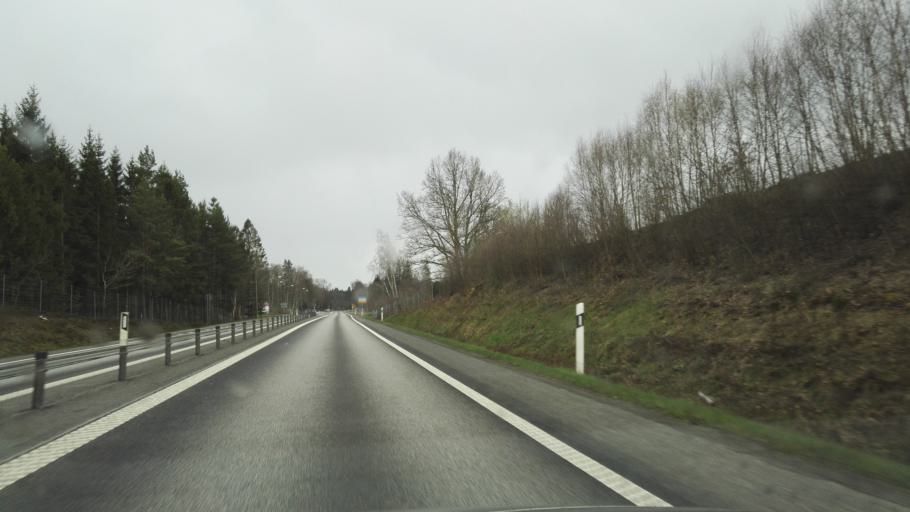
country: SE
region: Skane
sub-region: Osby Kommun
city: Osby
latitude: 56.3072
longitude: 14.0068
